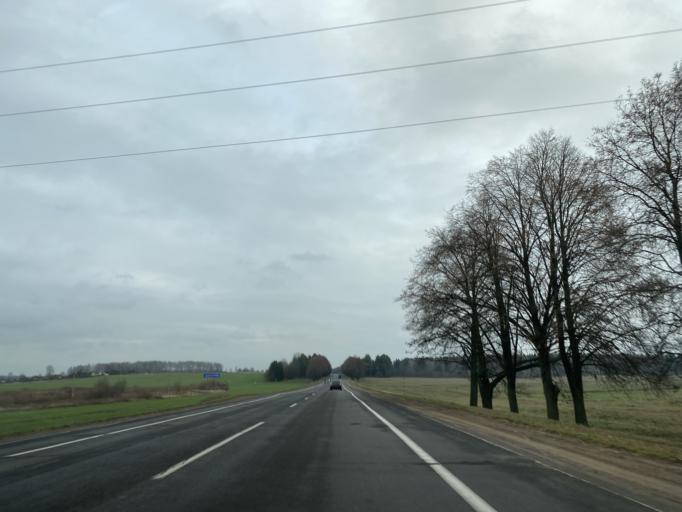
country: BY
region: Minsk
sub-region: Smalyavitski Rayon
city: Oktjabr'skij
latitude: 54.0729
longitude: 28.1972
